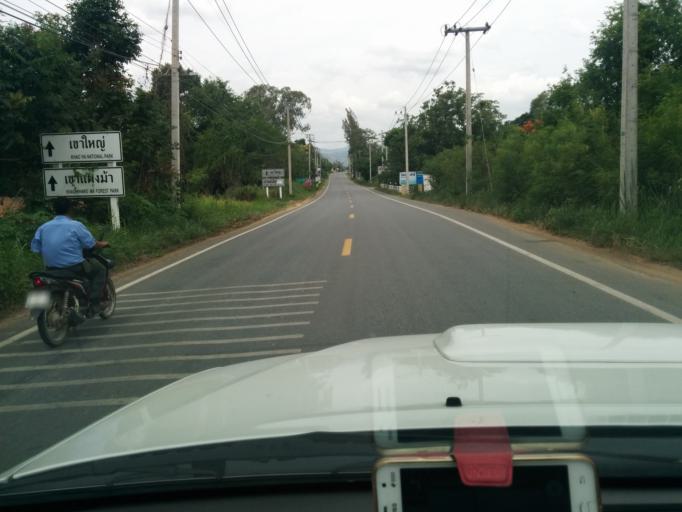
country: TH
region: Sara Buri
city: Muak Lek
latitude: 14.5954
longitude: 101.2177
